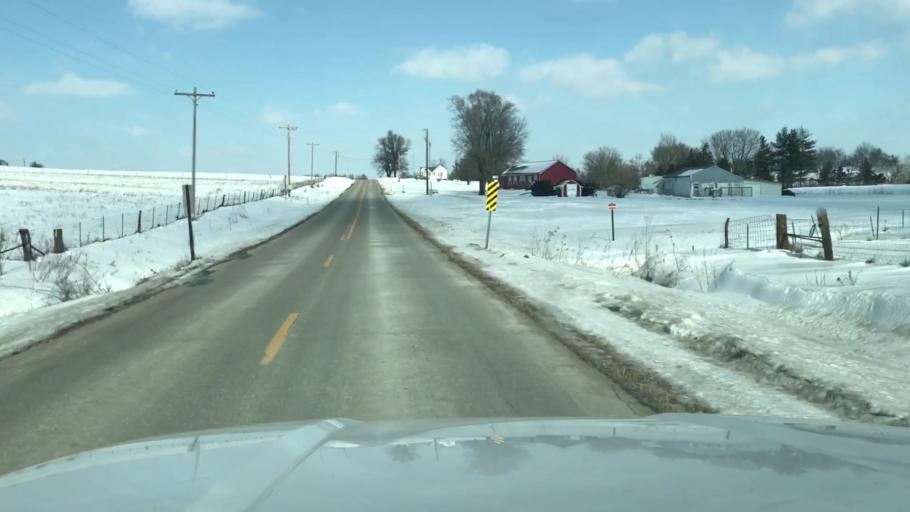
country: US
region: Missouri
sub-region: Nodaway County
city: Maryville
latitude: 40.3453
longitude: -94.7224
